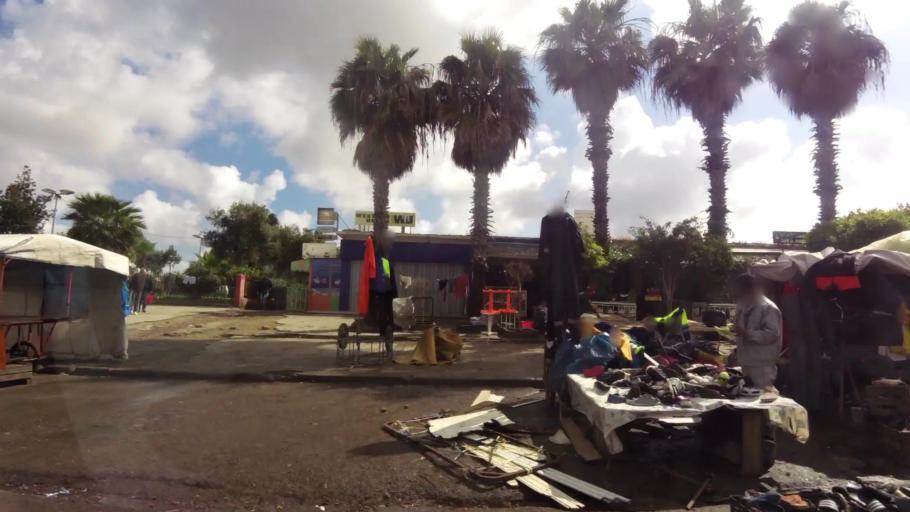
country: MA
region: Grand Casablanca
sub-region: Casablanca
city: Casablanca
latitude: 33.5331
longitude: -7.6702
